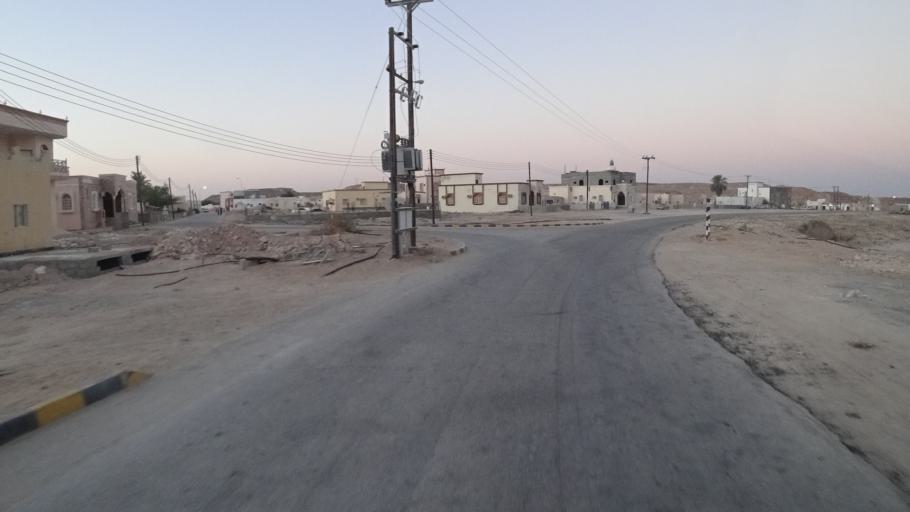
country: OM
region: Zufar
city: Salalah
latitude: 17.4854
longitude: 53.3491
